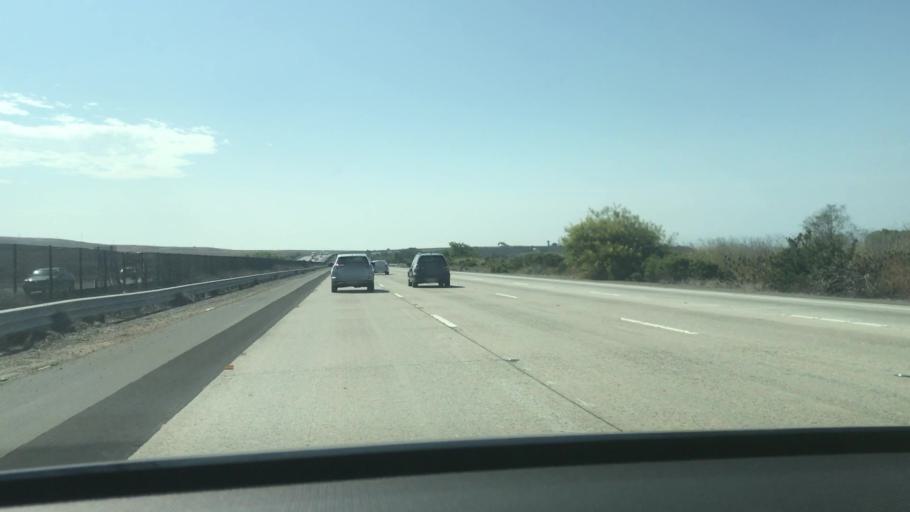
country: US
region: California
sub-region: San Diego County
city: Camp Pendleton South
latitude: 33.3279
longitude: -117.4914
